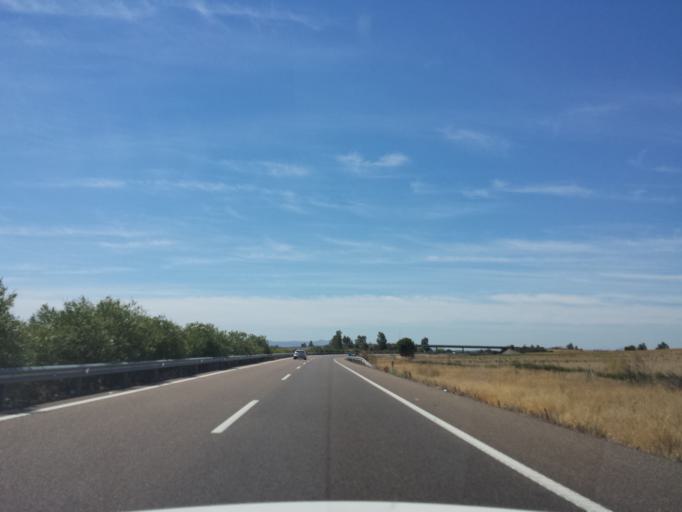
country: ES
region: Extremadura
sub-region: Provincia de Badajoz
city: Santa Amalia
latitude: 38.9980
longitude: -6.0944
